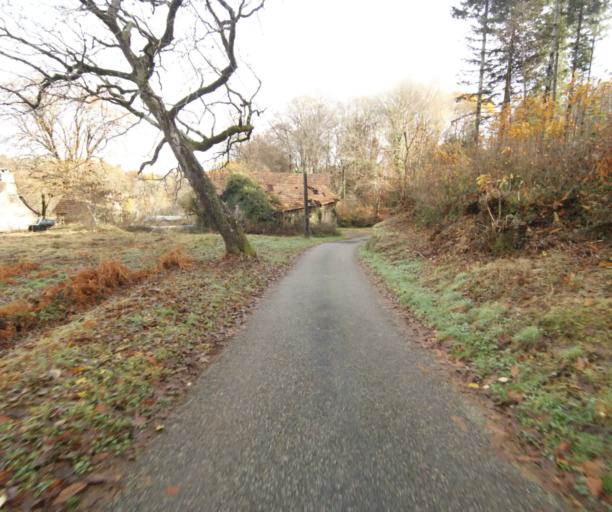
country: FR
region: Limousin
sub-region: Departement de la Correze
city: Sainte-Fortunade
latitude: 45.2034
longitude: 1.7357
